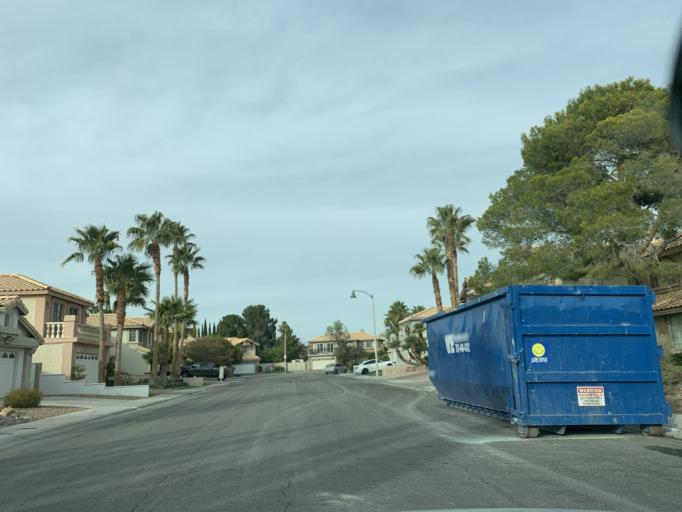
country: US
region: Nevada
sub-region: Clark County
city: Summerlin South
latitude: 36.1416
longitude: -115.2999
